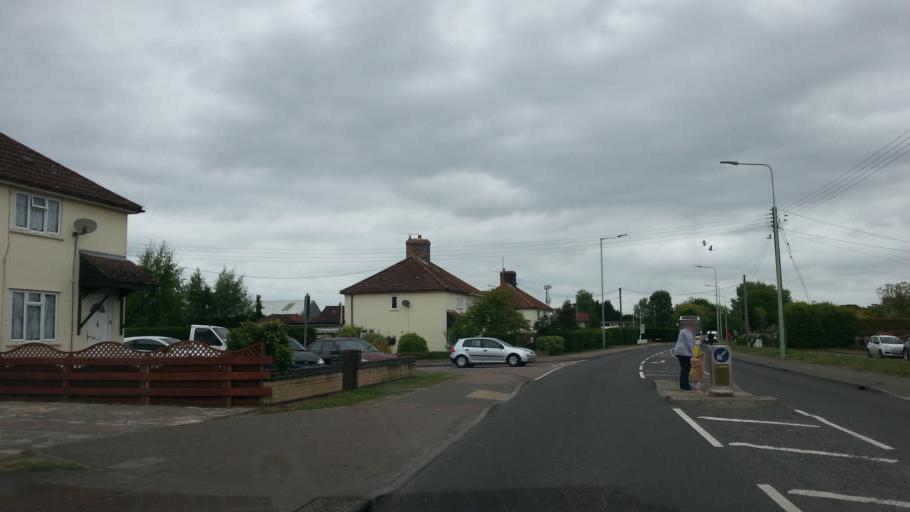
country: GB
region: England
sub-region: Suffolk
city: Lakenheath
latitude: 52.3500
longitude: 0.5116
